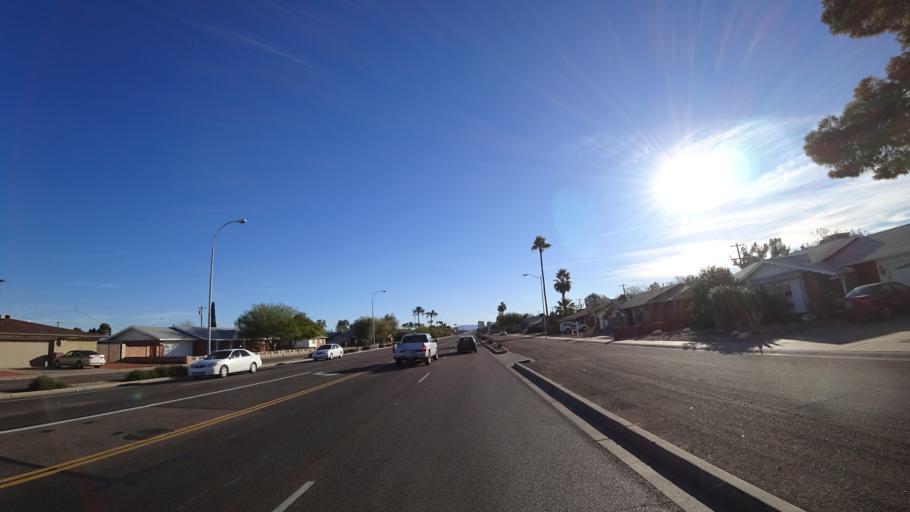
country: US
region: Arizona
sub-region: Maricopa County
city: Scottsdale
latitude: 33.4803
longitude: -111.9000
